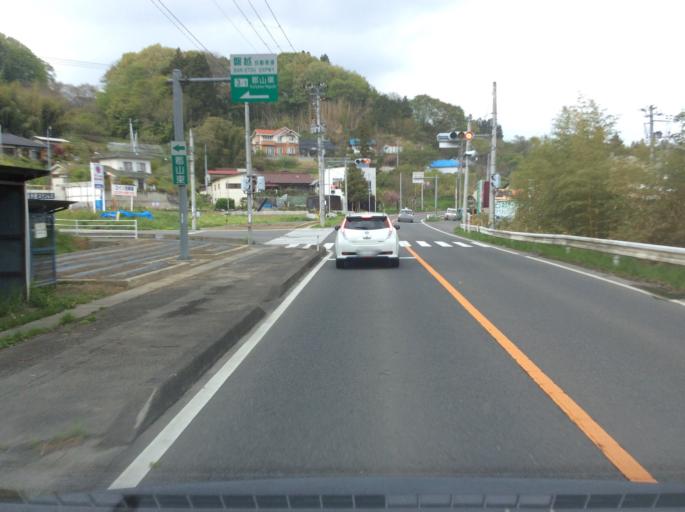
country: JP
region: Fukushima
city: Miharu
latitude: 37.4270
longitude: 140.4569
